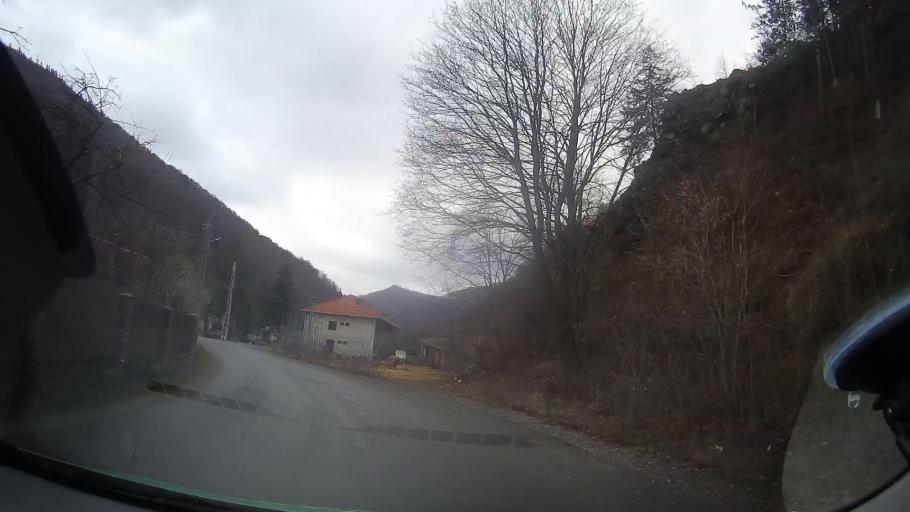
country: RO
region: Cluj
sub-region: Comuna Valea Ierii
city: Valea Ierii
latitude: 46.6475
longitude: 23.3388
